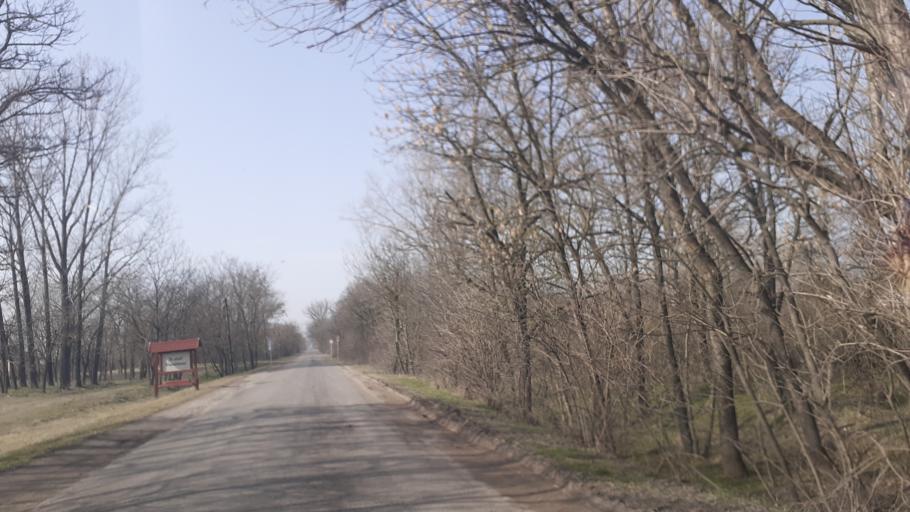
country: HU
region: Pest
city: Dabas
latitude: 47.0652
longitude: 19.2765
